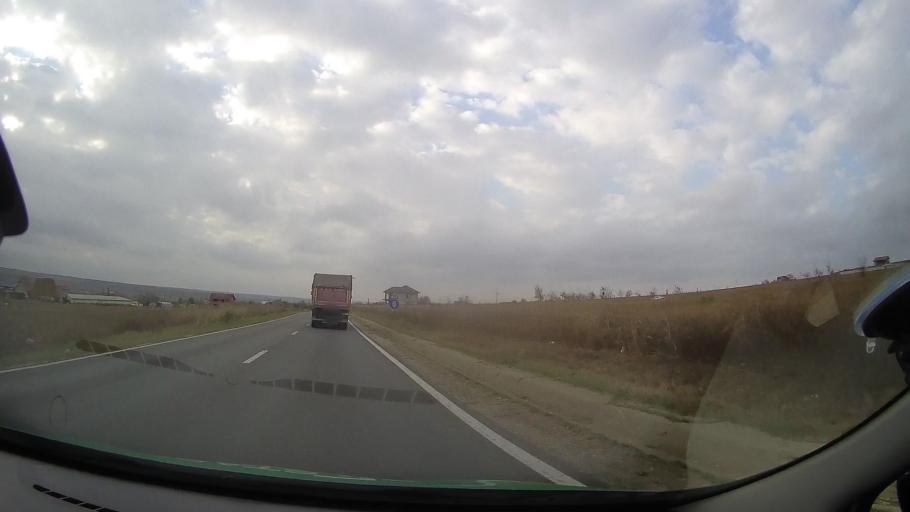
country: RO
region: Constanta
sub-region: Comuna Mircea Voda
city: Satu Nou
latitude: 44.2655
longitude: 28.2384
